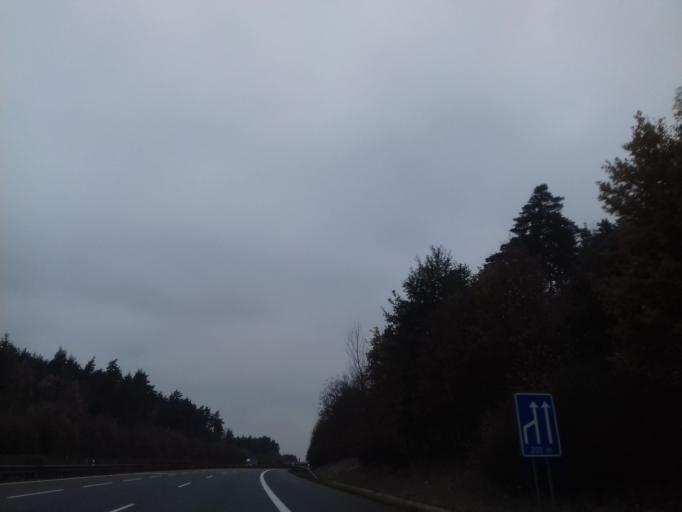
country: CZ
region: Plzensky
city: Dobrany
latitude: 49.6828
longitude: 13.3034
